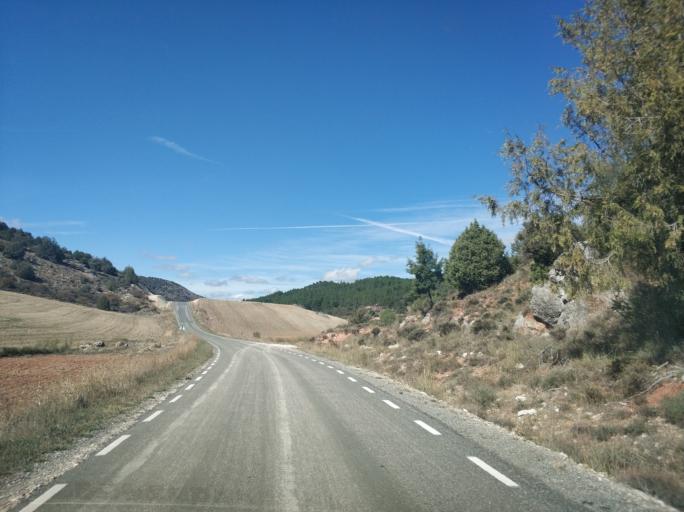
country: ES
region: Castille and Leon
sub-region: Provincia de Soria
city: Espeja de San Marcelino
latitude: 41.8128
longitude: -3.2254
